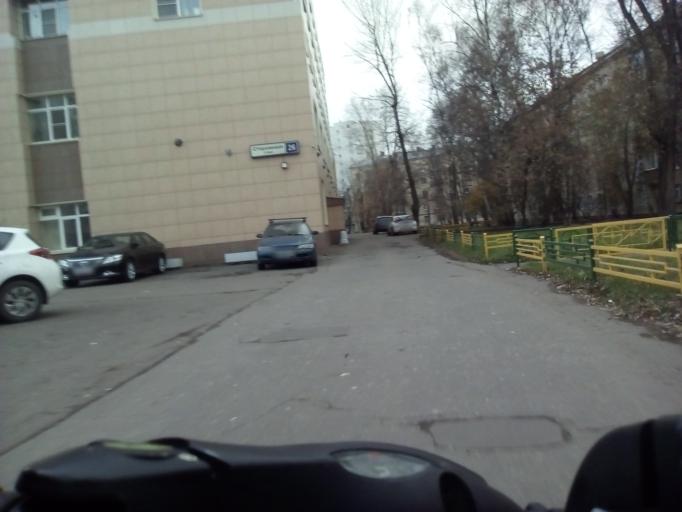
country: RU
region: Moscow
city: Lefortovo
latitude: 55.7661
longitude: 37.7132
